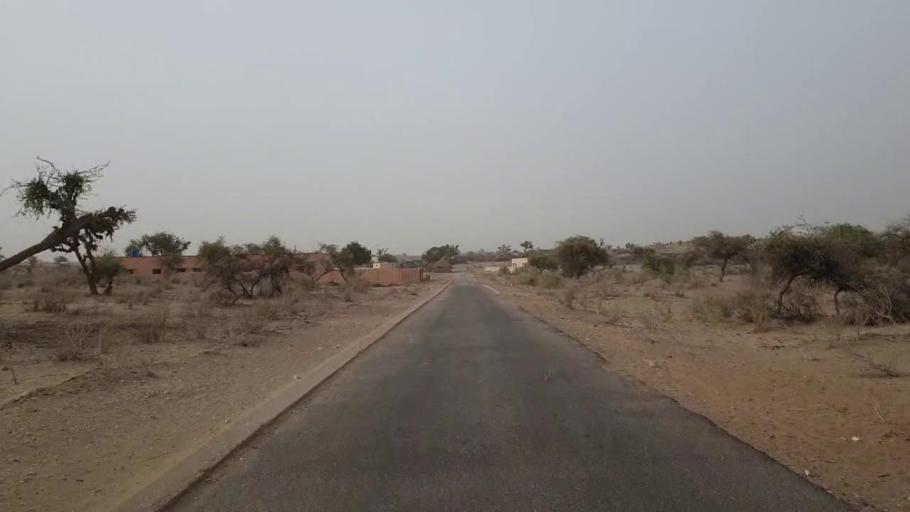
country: PK
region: Sindh
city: Islamkot
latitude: 24.5726
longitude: 70.3653
